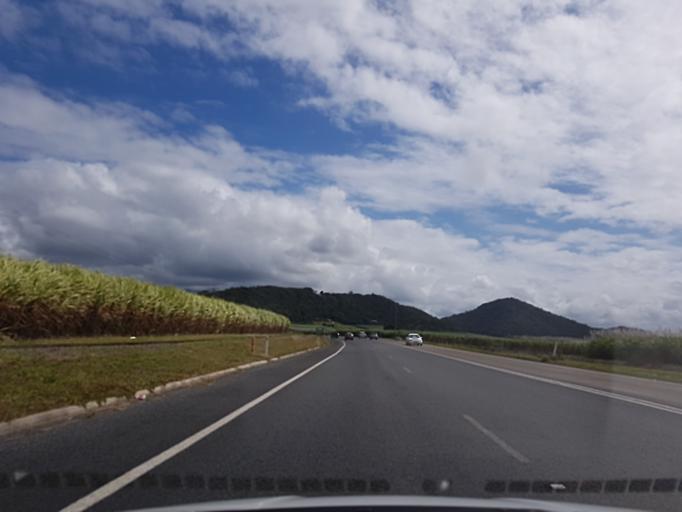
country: AU
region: Queensland
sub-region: Cairns
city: Port Douglas
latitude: -16.4792
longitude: 145.4057
